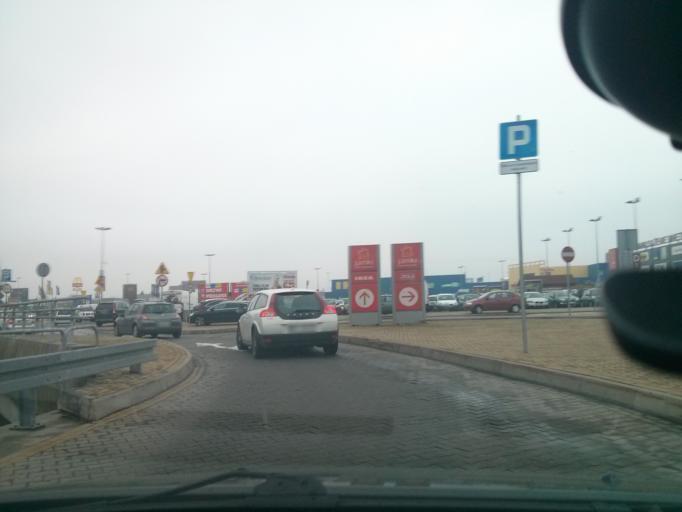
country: PL
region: Masovian Voivodeship
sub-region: Powiat pruszkowski
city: Nowe Grocholice
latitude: 52.1348
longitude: 20.8986
